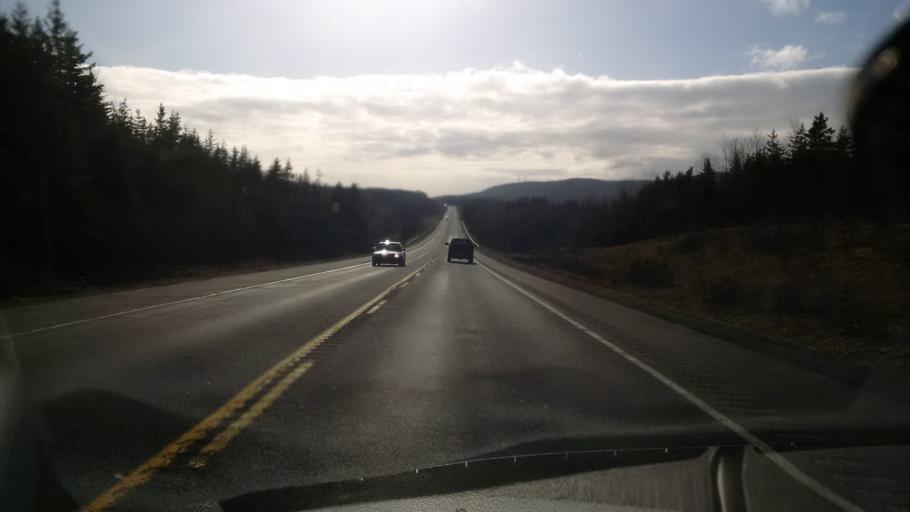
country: CA
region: Nova Scotia
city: Antigonish
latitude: 45.5873
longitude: -62.3012
